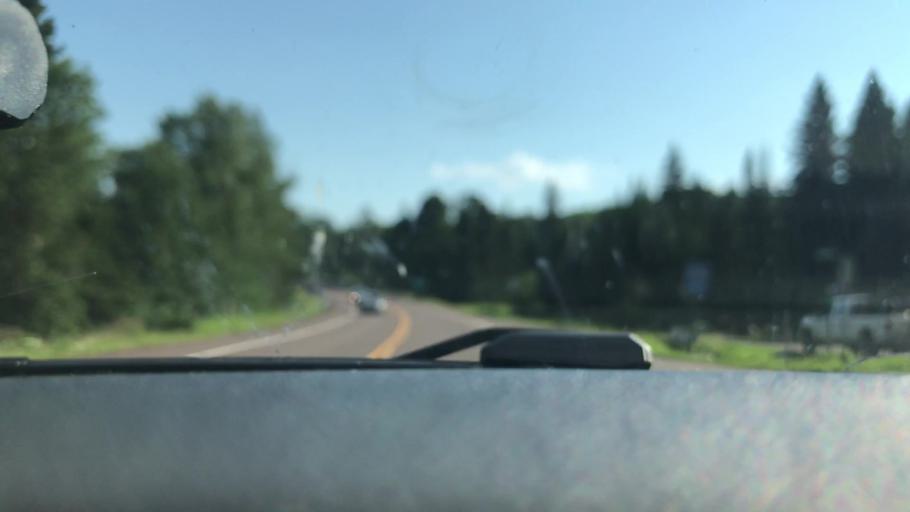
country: US
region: Minnesota
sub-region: Cook County
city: Grand Marais
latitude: 47.8389
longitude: -89.9720
